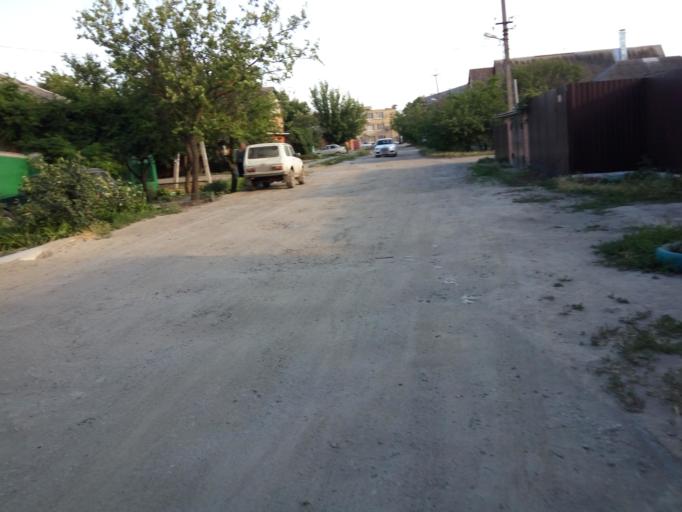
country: RU
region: Rostov
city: Bataysk
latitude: 47.1165
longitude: 39.7356
